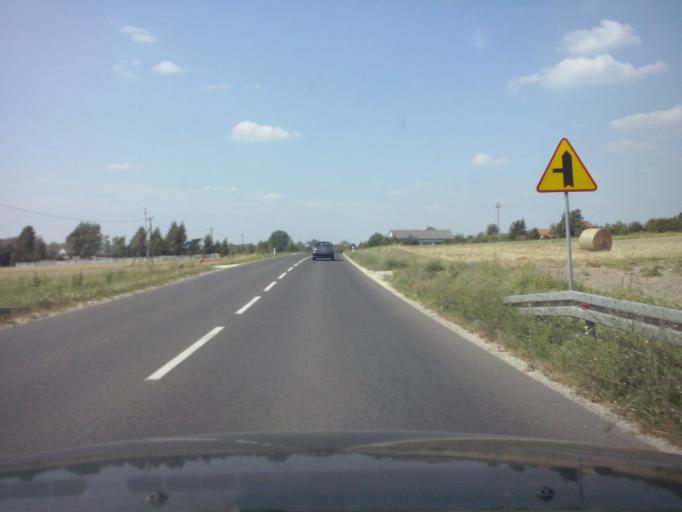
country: PL
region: Swietokrzyskie
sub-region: Powiat buski
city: Gnojno
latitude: 50.5890
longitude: 20.8993
